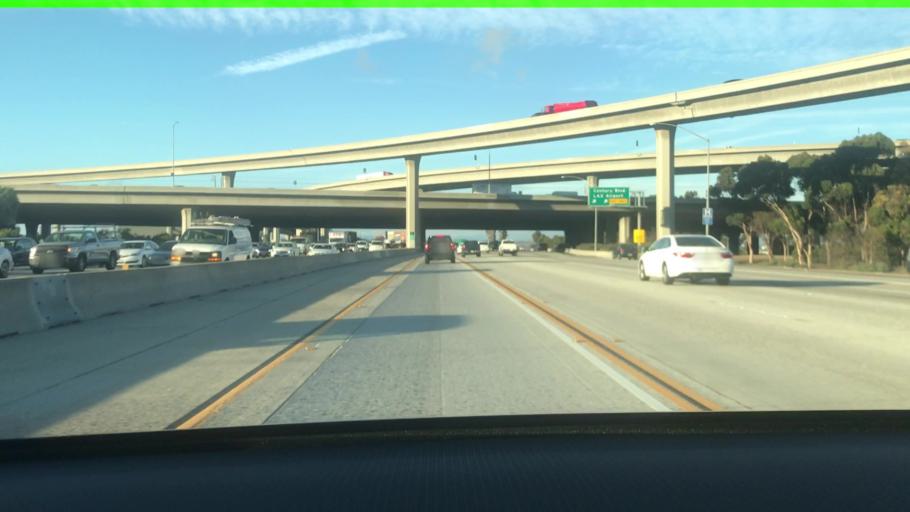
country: US
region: California
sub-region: Los Angeles County
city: Del Aire
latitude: 33.9284
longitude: -118.3683
